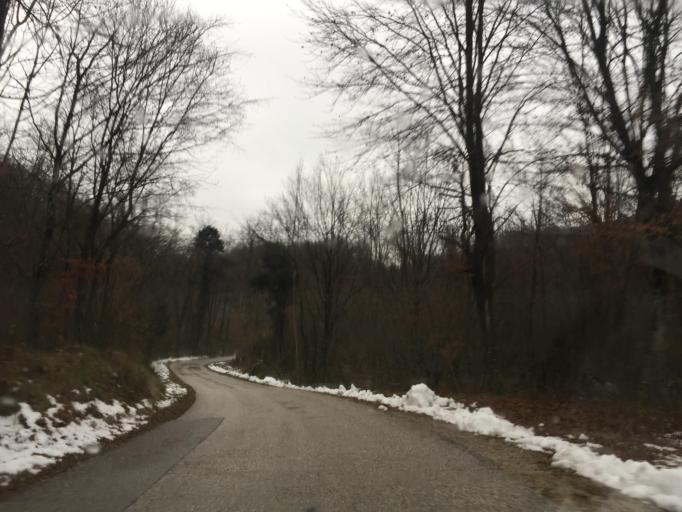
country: SI
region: Kanal
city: Kanal
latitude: 46.0647
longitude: 13.6621
